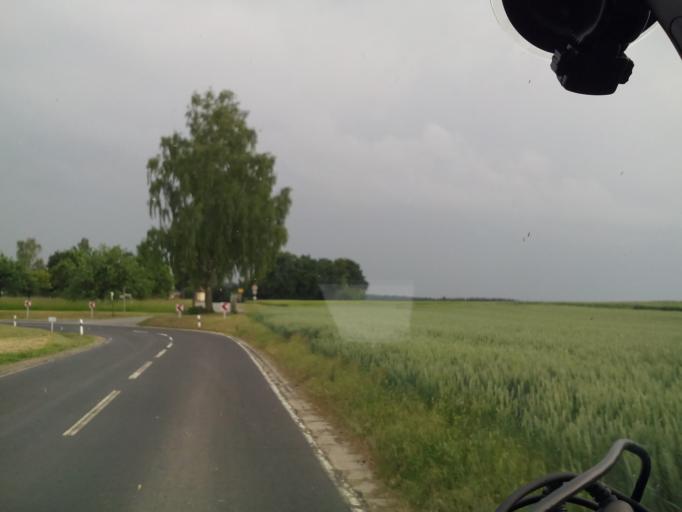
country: DE
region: Bavaria
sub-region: Regierungsbezirk Unterfranken
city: Hendungen
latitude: 50.3959
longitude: 10.3469
